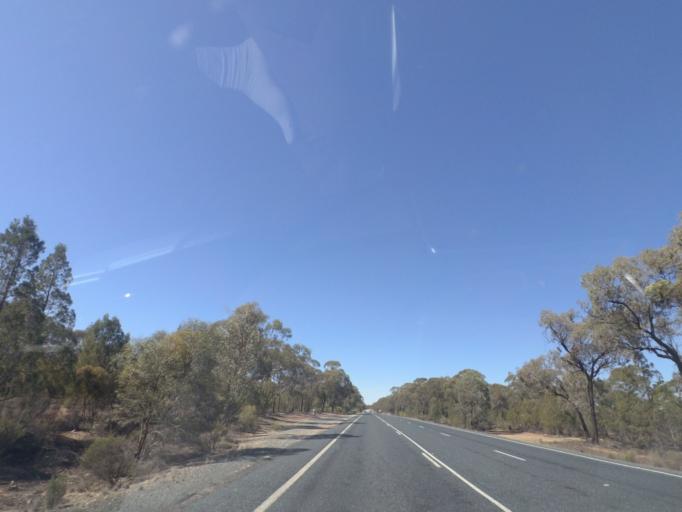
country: AU
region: New South Wales
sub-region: Bland
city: West Wyalong
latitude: -34.1304
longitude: 147.1238
